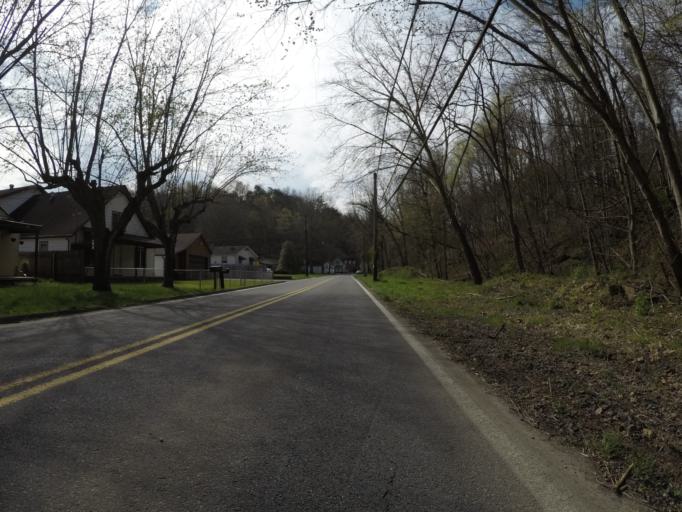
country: US
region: West Virginia
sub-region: Cabell County
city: Pea Ridge
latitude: 38.3751
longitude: -82.3709
